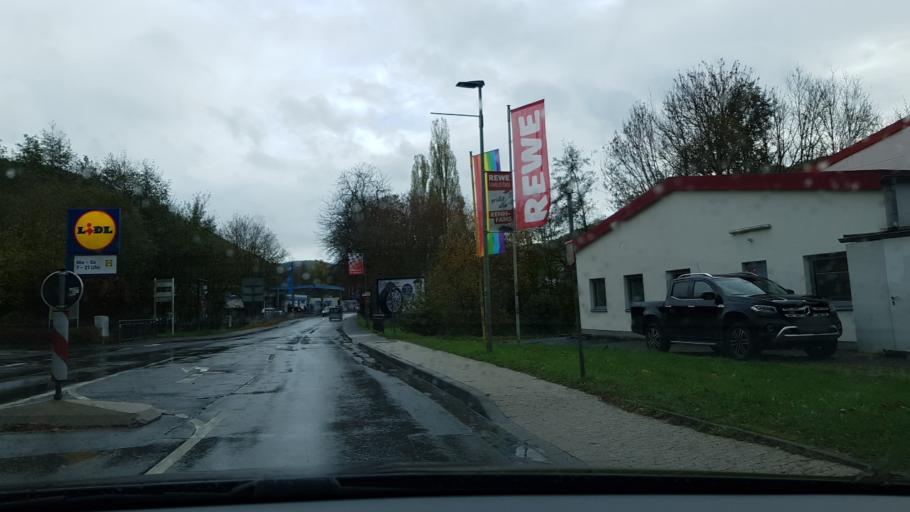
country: DE
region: Rheinland-Pfalz
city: Adenau
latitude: 50.3792
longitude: 6.9480
